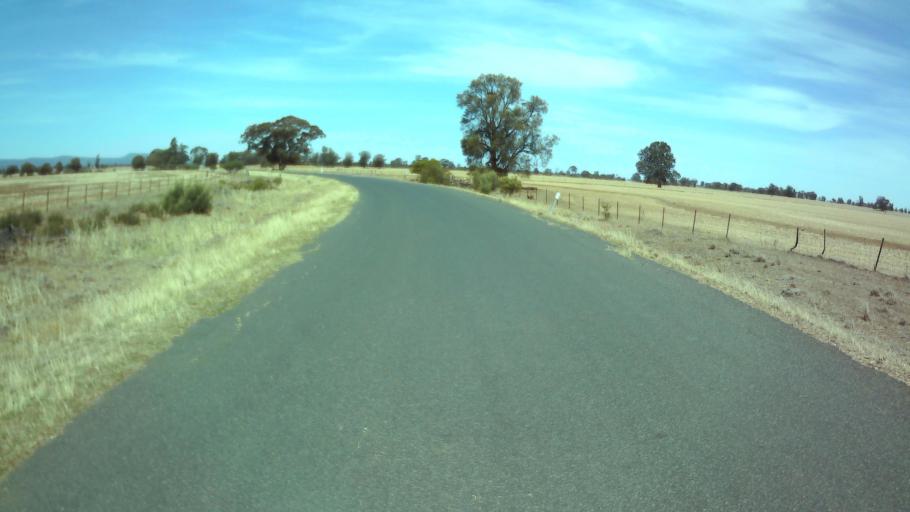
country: AU
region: New South Wales
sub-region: Weddin
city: Grenfell
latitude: -33.9398
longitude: 147.7636
